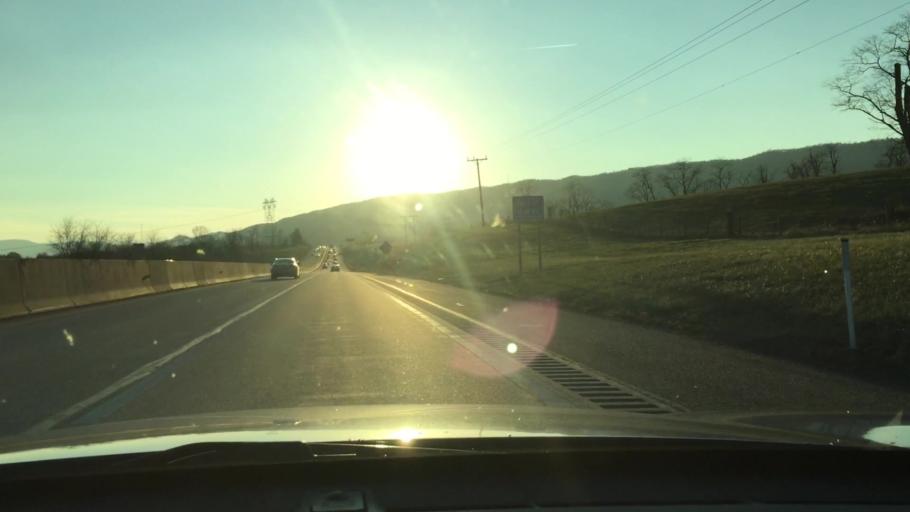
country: US
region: Pennsylvania
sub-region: Franklin County
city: Doylestown
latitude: 40.1080
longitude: -77.7975
